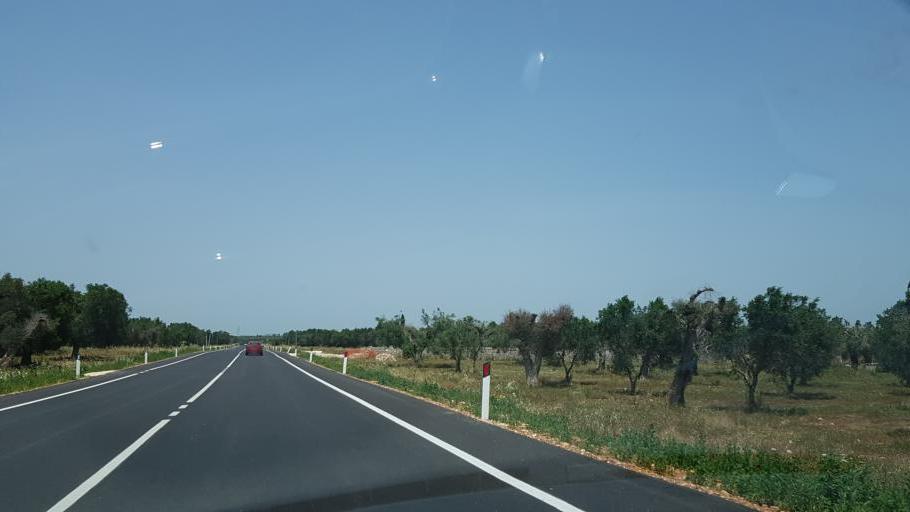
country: IT
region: Apulia
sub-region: Provincia di Brindisi
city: San Pancrazio Salentino
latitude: 40.4690
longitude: 17.8382
